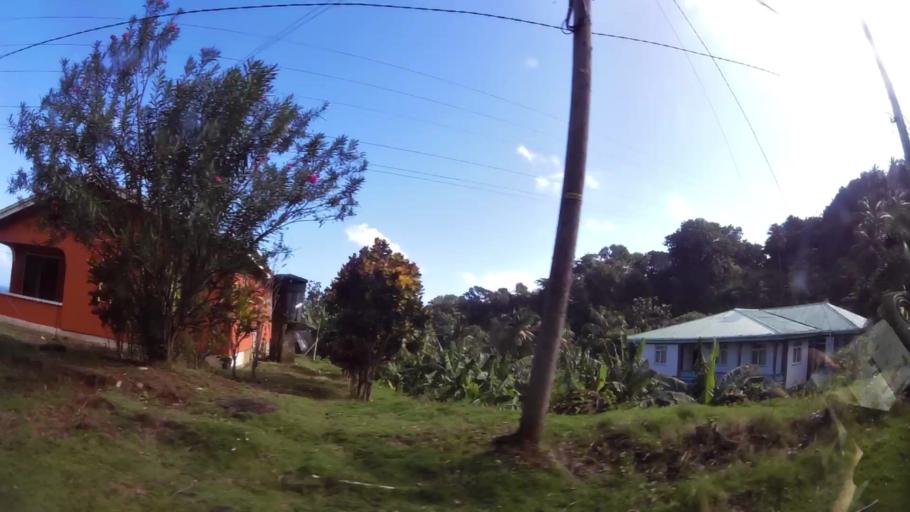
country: DM
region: Saint Andrew
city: Marigot
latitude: 15.5183
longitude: -61.2668
